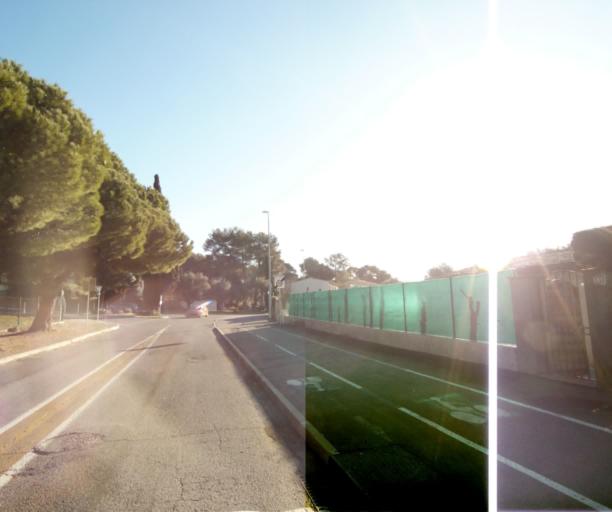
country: FR
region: Provence-Alpes-Cote d'Azur
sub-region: Departement des Alpes-Maritimes
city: Vallauris
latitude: 43.5969
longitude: 7.0757
